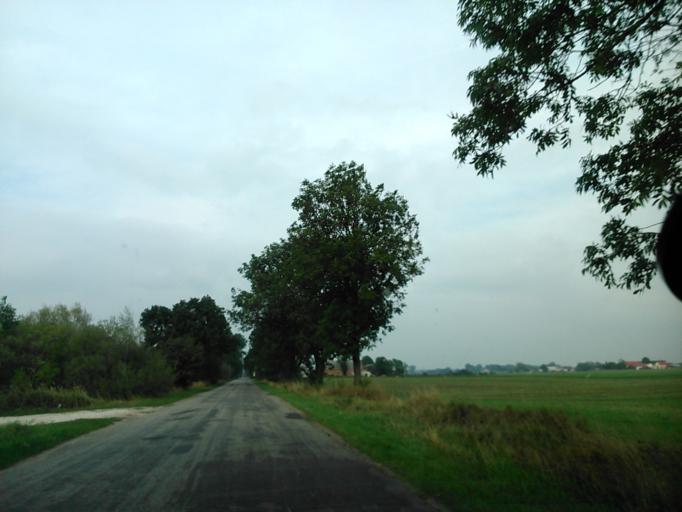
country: PL
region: Kujawsko-Pomorskie
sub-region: Powiat wabrzeski
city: Pluznica
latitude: 53.2464
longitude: 18.8220
